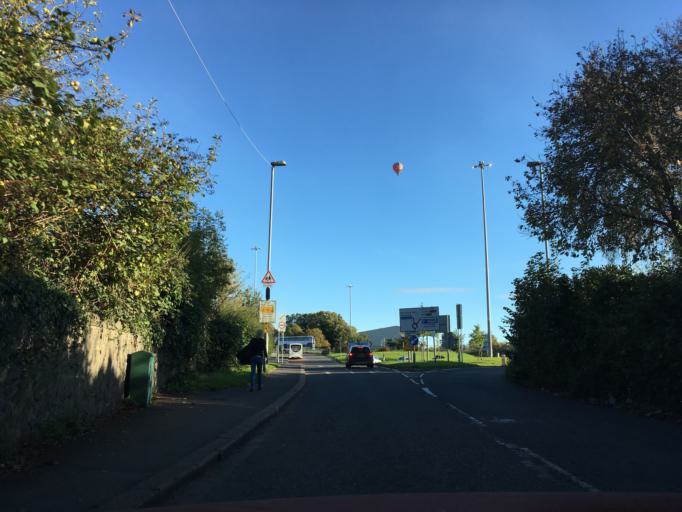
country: GB
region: England
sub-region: Bristol
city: Bristol
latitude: 51.4421
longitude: -2.6277
